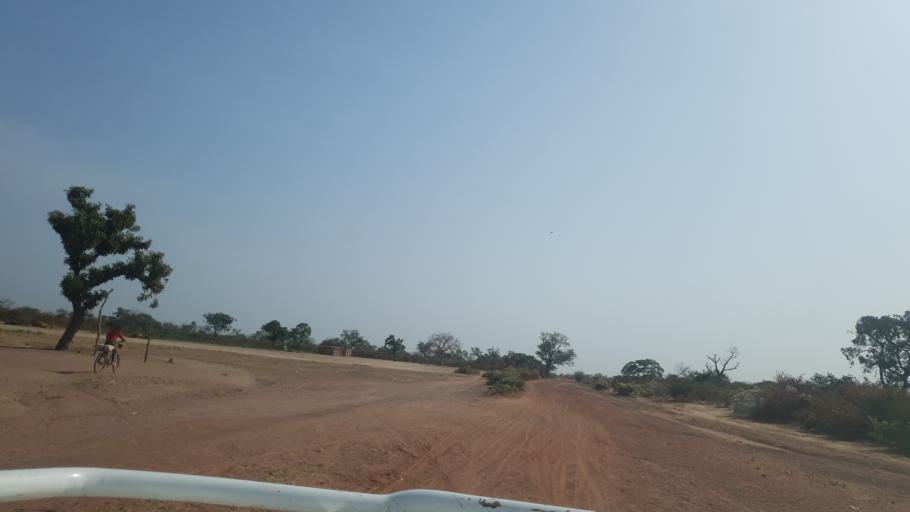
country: ML
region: Koulikoro
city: Dioila
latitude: 12.6693
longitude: -6.6702
